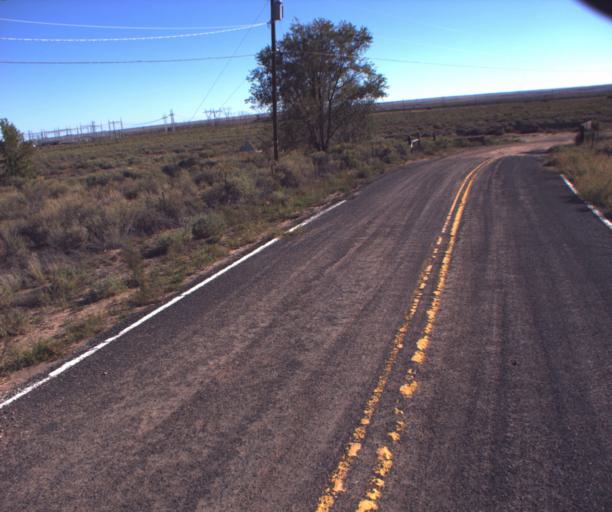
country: US
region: Arizona
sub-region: Navajo County
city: Joseph City
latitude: 34.9502
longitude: -110.3122
